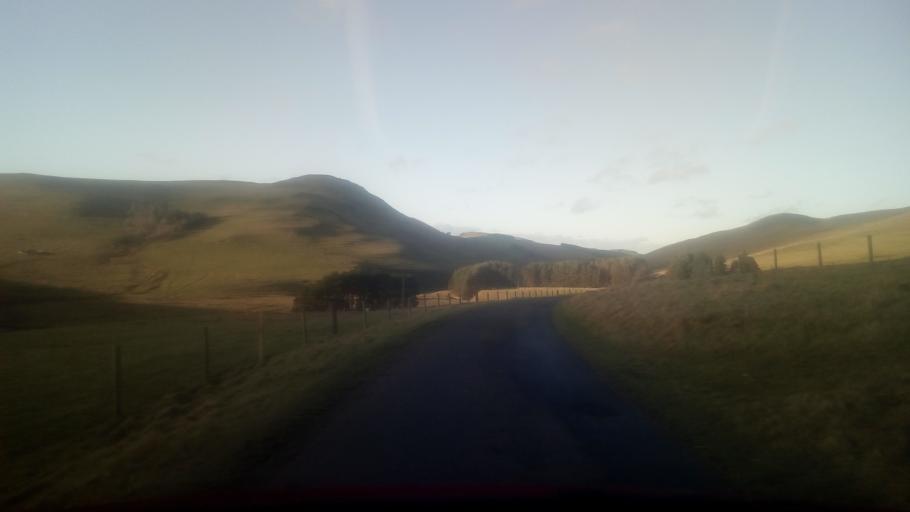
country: GB
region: Scotland
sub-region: The Scottish Borders
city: Kelso
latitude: 55.4344
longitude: -2.3641
